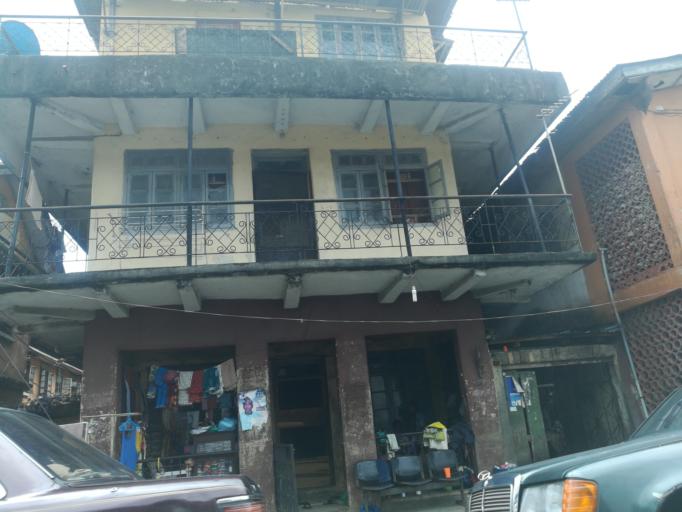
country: NG
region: Lagos
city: Mushin
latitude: 6.5237
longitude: 3.3657
